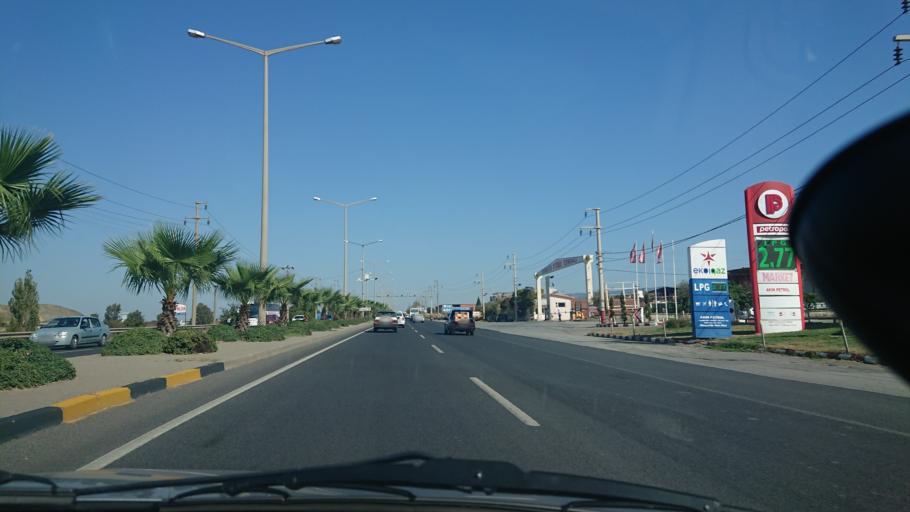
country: TR
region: Manisa
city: Turgutlu
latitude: 38.4957
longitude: 27.7369
